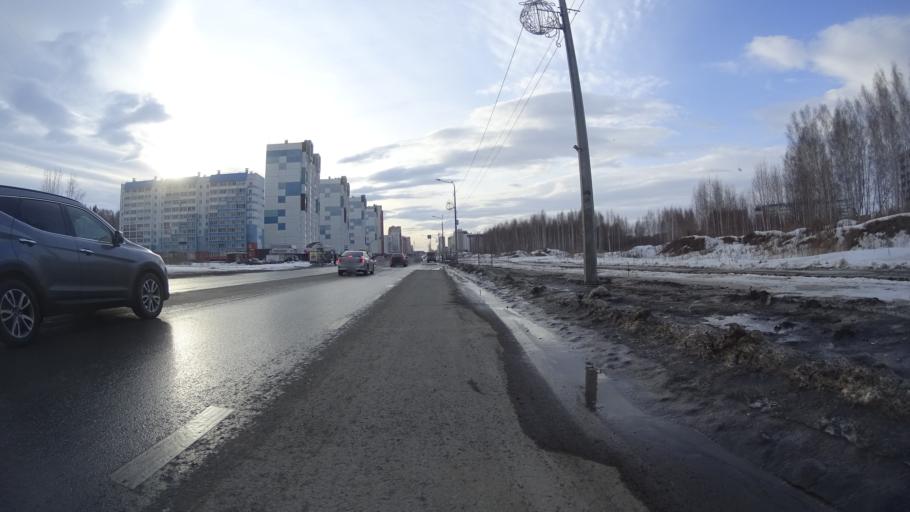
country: RU
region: Chelyabinsk
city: Roshchino
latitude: 55.2090
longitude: 61.2995
